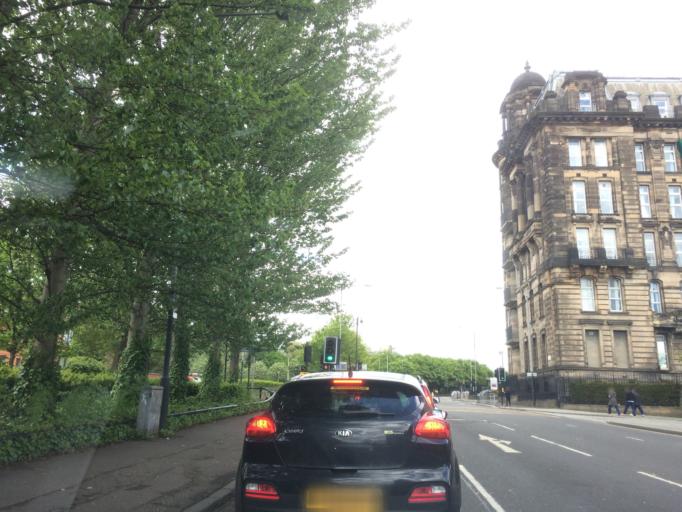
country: GB
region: Scotland
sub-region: Glasgow City
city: Glasgow
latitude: 55.8628
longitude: -4.2368
